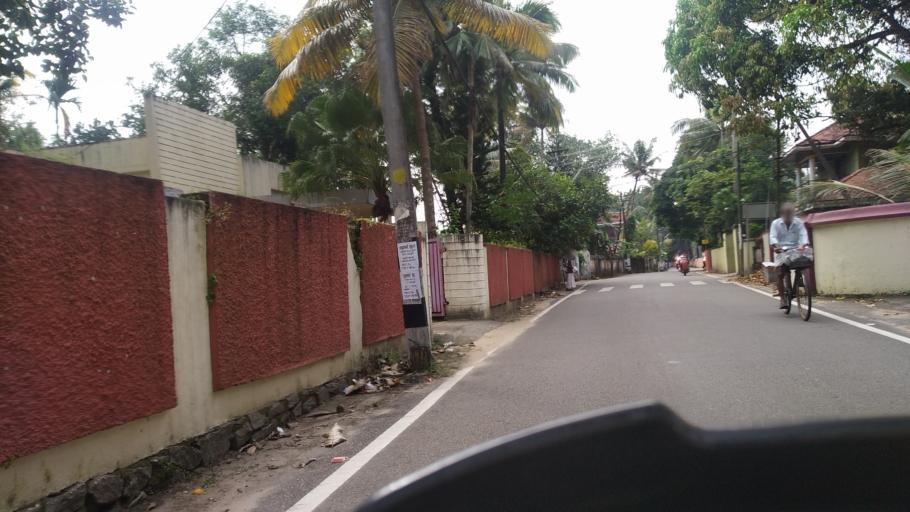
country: IN
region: Kerala
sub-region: Thrissur District
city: Kodungallur
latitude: 10.1432
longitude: 76.2330
